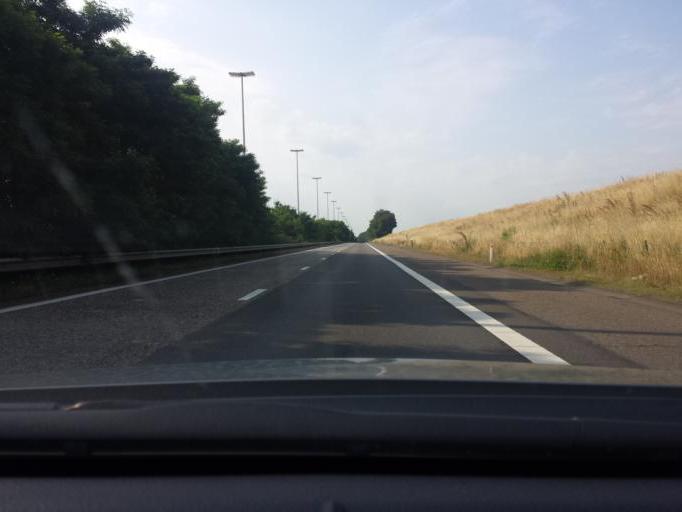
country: BE
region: Flanders
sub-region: Provincie Limburg
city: Hoeselt
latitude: 50.8161
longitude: 5.5149
